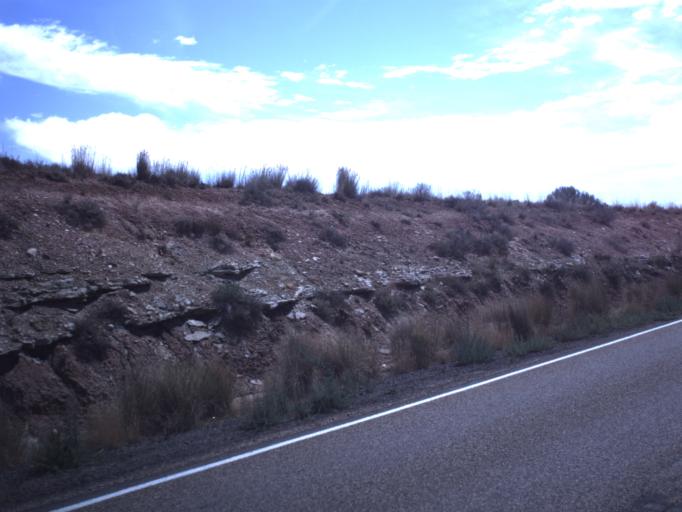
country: US
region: Utah
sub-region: Uintah County
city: Maeser
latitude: 40.3136
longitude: -109.6920
